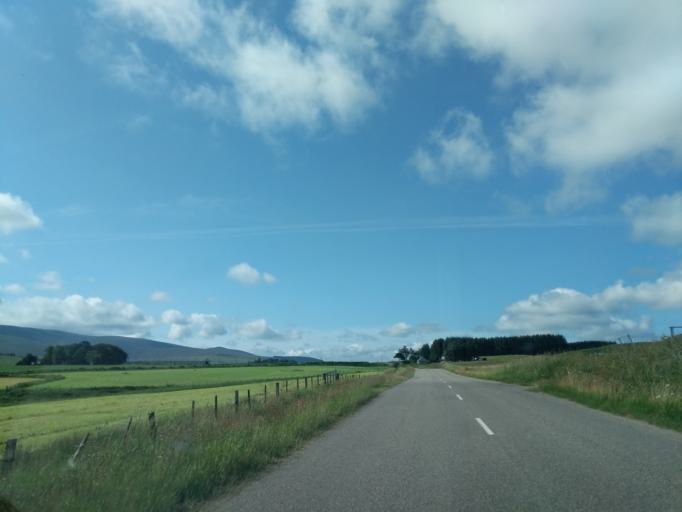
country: GB
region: Scotland
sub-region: Moray
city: Dufftown
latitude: 57.4033
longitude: -3.1876
